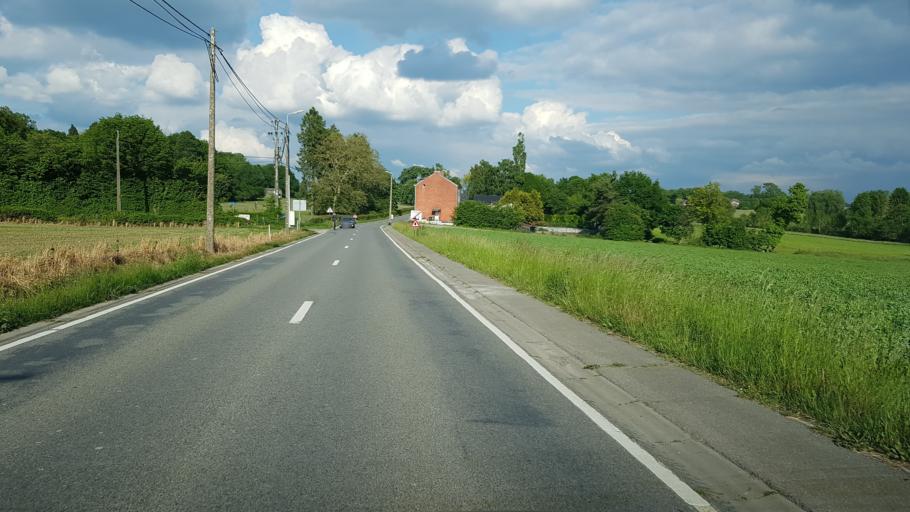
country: BE
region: Wallonia
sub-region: Province de Liege
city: Sprimont
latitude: 50.5391
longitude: 5.6431
